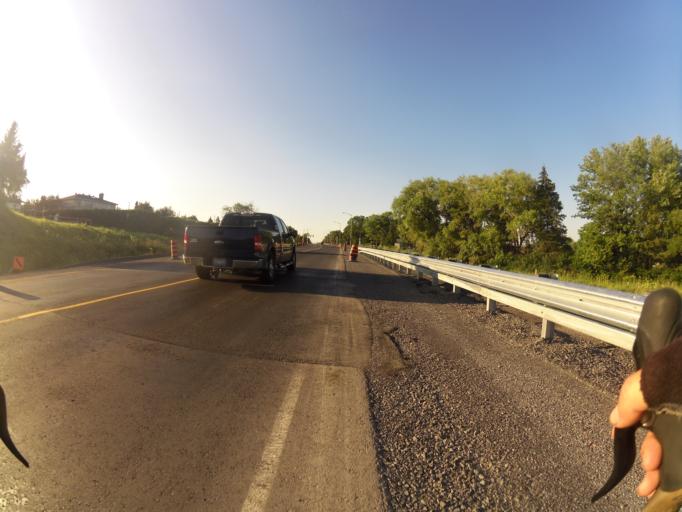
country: CA
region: Ontario
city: Ottawa
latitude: 45.2935
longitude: -75.7013
